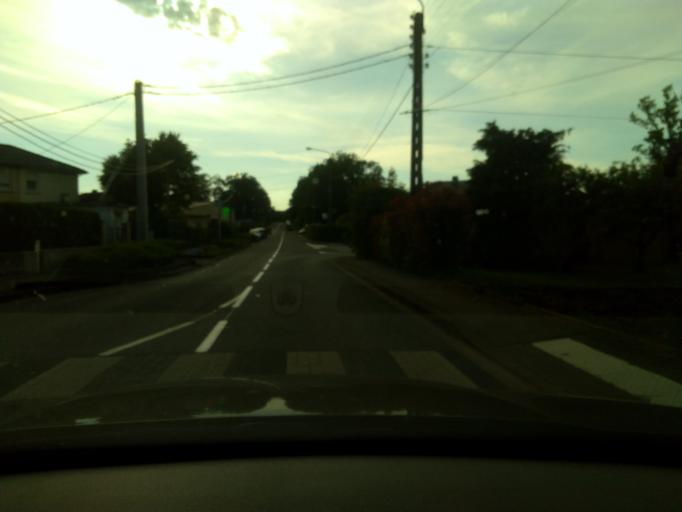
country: FR
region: Lorraine
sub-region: Departement de la Moselle
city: Seremange-Erzange
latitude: 49.3145
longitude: 6.0776
